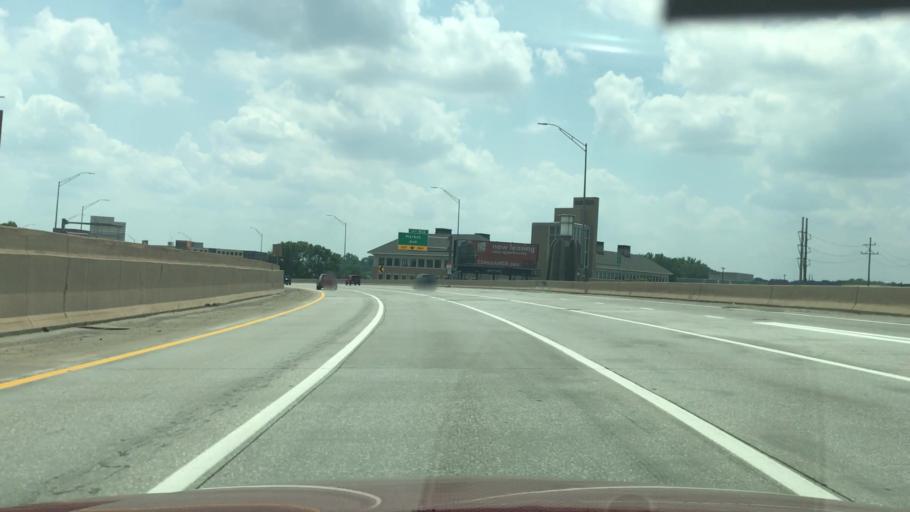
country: US
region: Michigan
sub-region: Kent County
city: Grand Rapids
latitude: 42.9643
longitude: -85.6789
